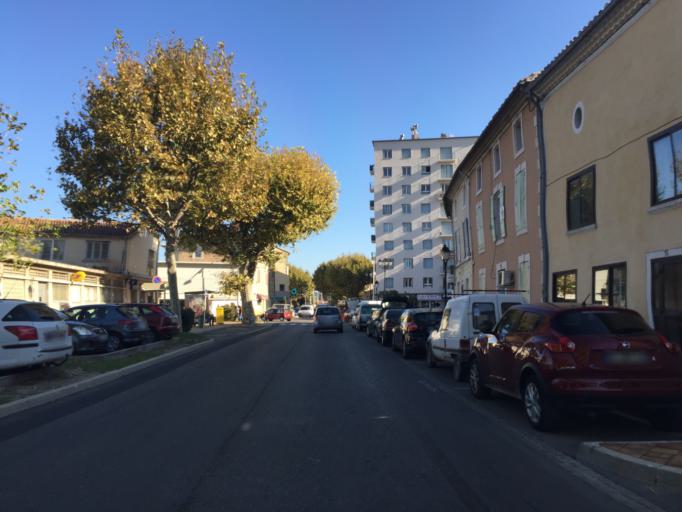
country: FR
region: Provence-Alpes-Cote d'Azur
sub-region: Departement du Vaucluse
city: Bollene
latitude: 44.2800
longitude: 4.7460
